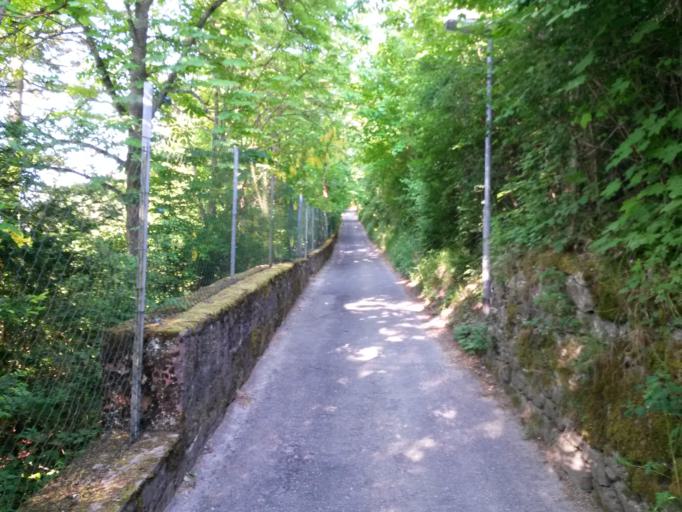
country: DE
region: Bavaria
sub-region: Regierungsbezirk Unterfranken
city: Bad Kissingen
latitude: 50.2027
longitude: 10.0662
